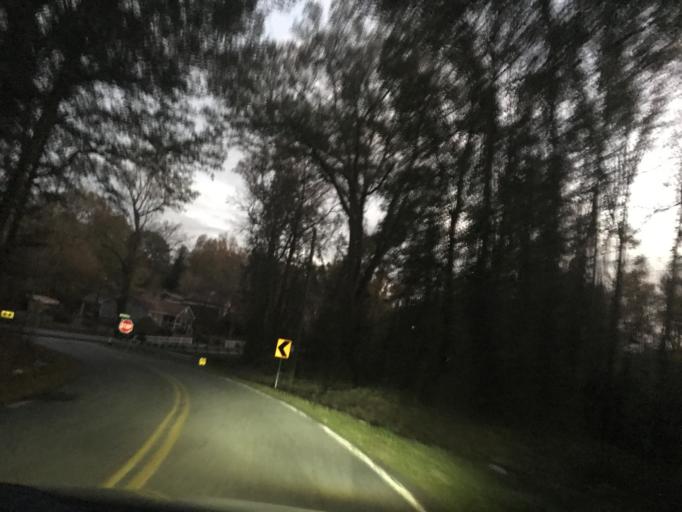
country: US
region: South Carolina
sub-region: Spartanburg County
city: Mayo
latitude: 35.0503
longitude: -81.8909
